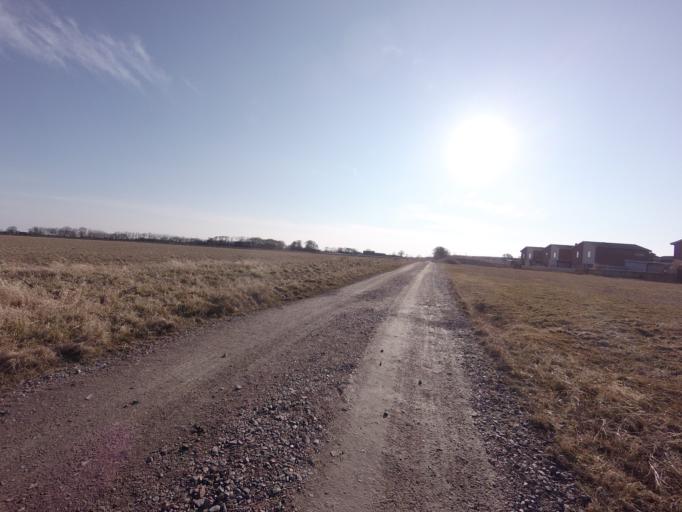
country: SE
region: Skane
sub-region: Hoganas Kommun
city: Hoganas
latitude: 56.1513
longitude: 12.5889
